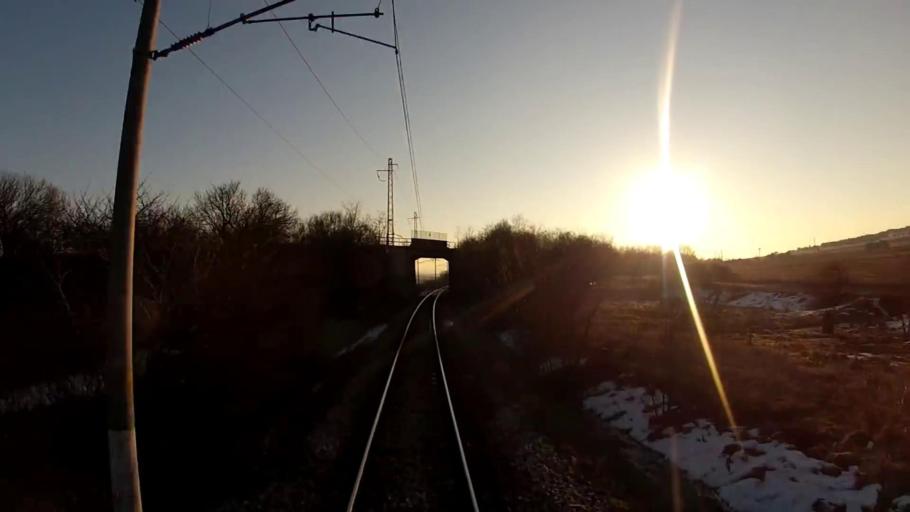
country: BG
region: Sofiya
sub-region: Obshtina Slivnitsa
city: Slivnitsa
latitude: 42.8771
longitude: 23.0169
